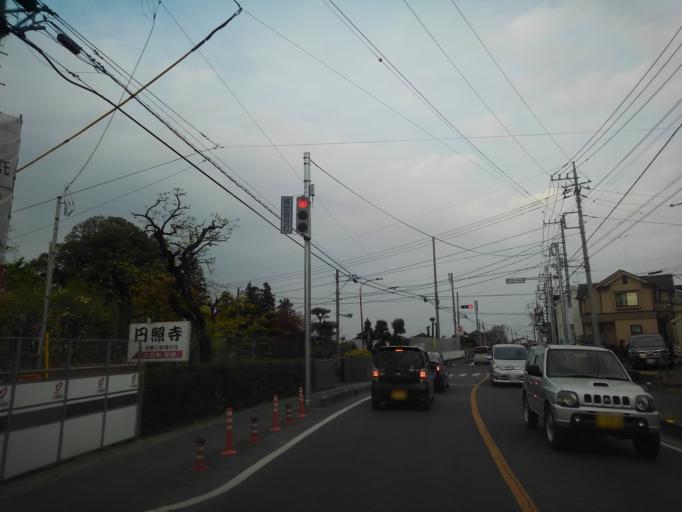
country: JP
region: Saitama
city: Hanno
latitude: 35.8354
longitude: 139.3474
